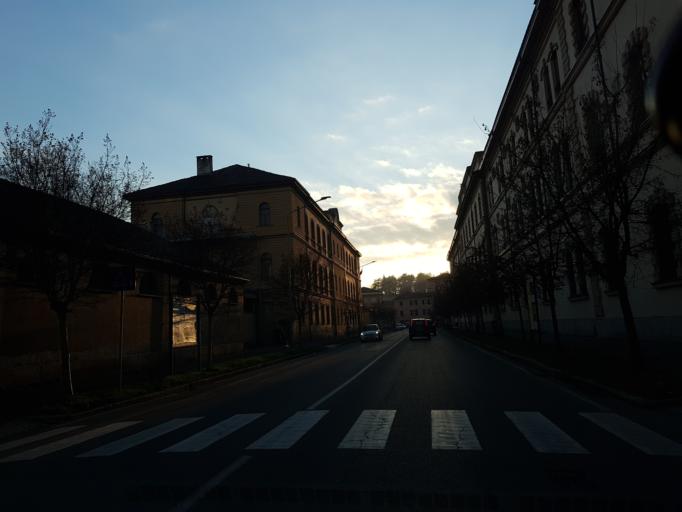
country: IT
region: Piedmont
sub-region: Provincia di Alessandria
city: Novi Ligure
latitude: 44.7621
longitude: 8.7942
